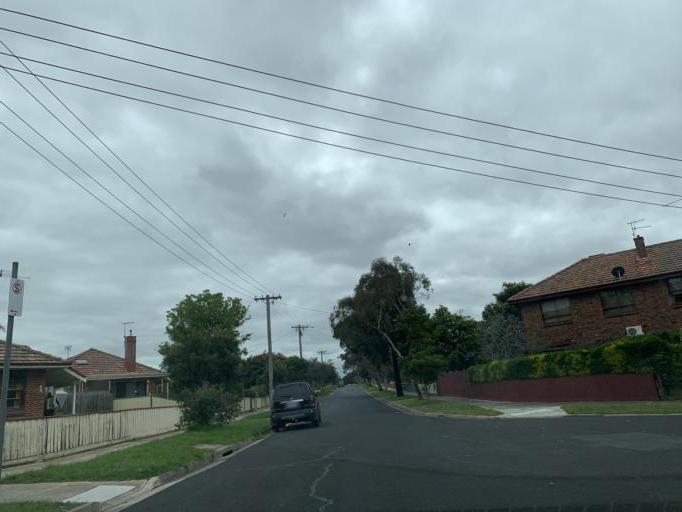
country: AU
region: Victoria
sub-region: Moreland
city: Coburg North
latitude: -37.7348
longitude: 144.9803
